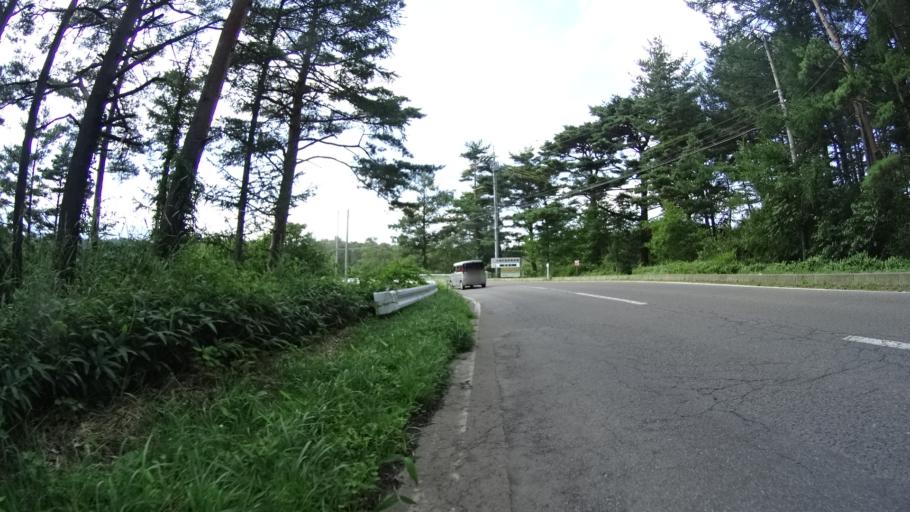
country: JP
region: Nagano
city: Saku
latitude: 36.0581
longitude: 138.4429
